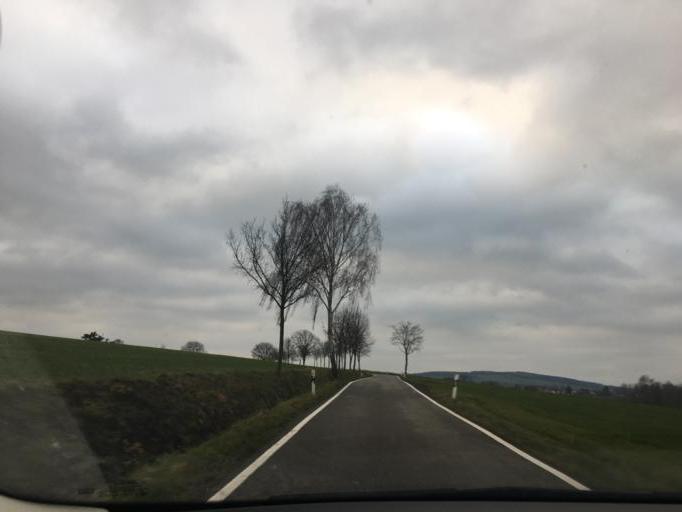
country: DE
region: Saxony
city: Niederfrohna
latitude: 50.8560
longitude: 12.7061
